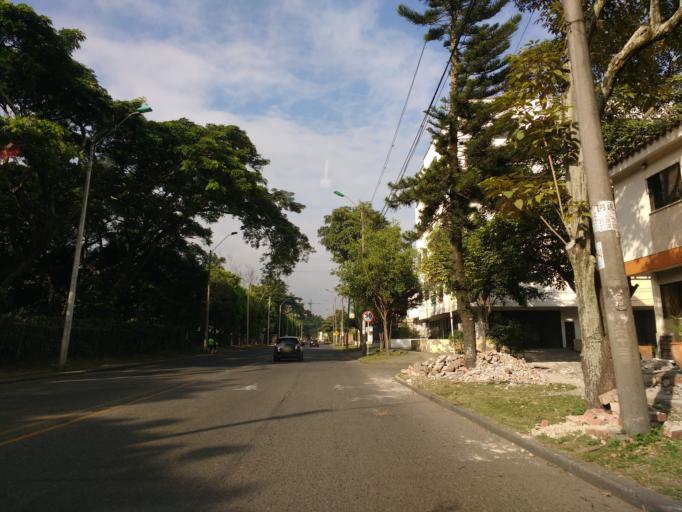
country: CO
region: Valle del Cauca
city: Cali
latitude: 3.4714
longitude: -76.5169
